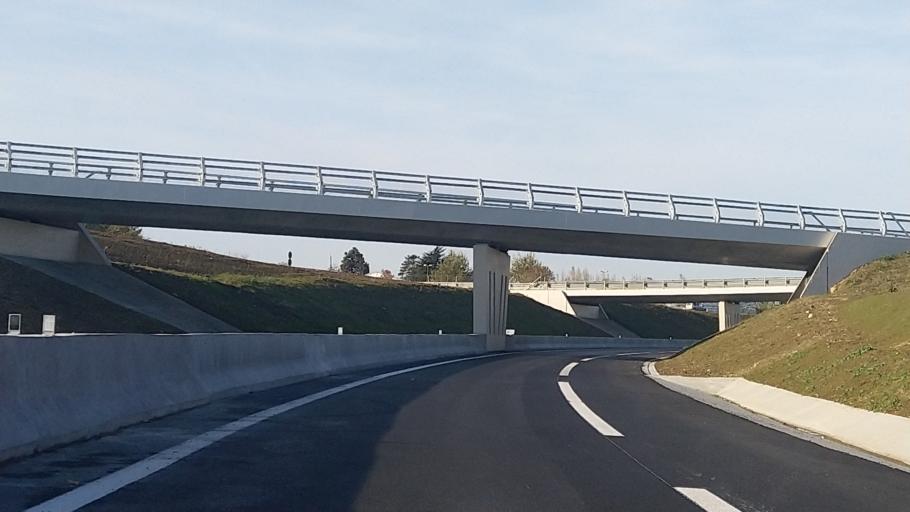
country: FR
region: Ile-de-France
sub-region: Departement du Val-d'Oise
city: Montsoult
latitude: 49.0652
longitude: 2.3322
